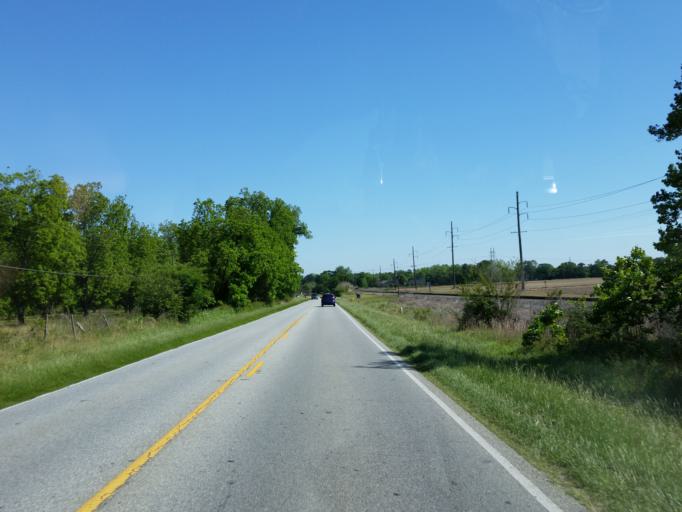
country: US
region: Georgia
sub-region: Lowndes County
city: Remerton
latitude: 30.9141
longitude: -83.3466
